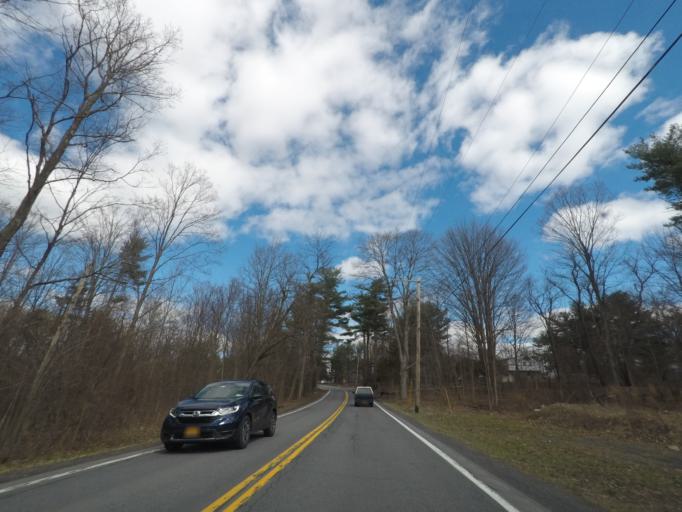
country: US
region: New York
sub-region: Albany County
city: Delmar
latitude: 42.5690
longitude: -73.8931
